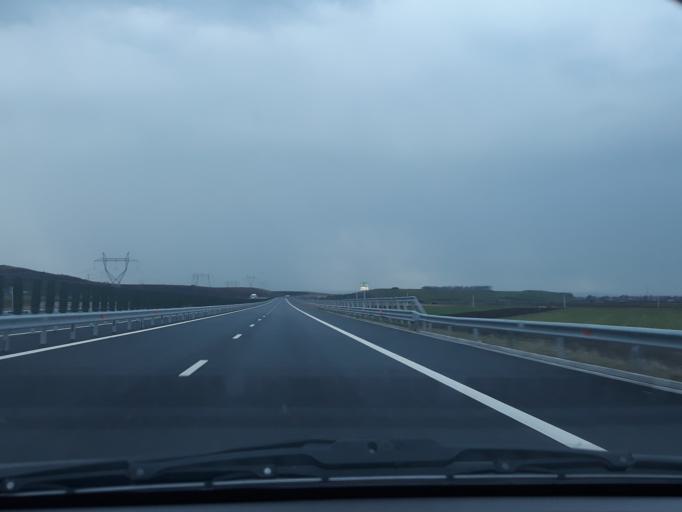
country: RO
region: Mures
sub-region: Comuna Sanpaul
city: Sanpaul
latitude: 46.4440
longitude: 24.3542
